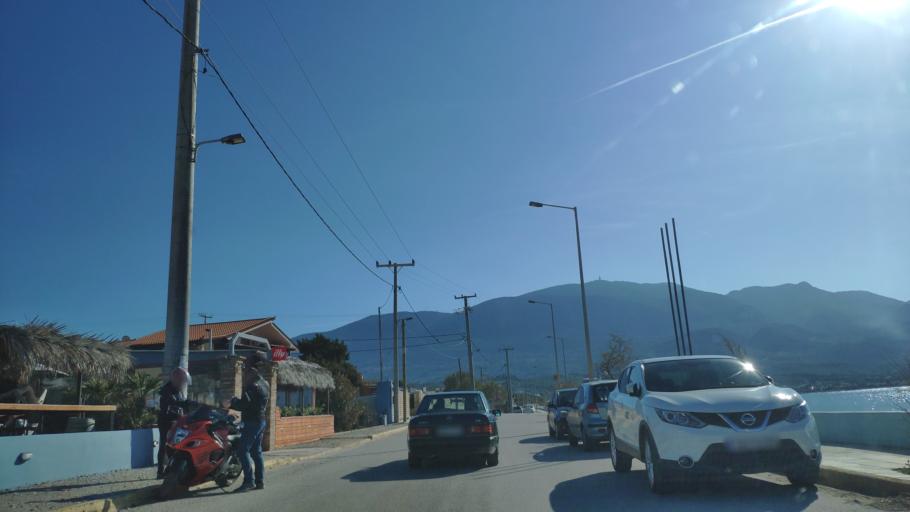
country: GR
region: Attica
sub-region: Nomarchia Dytikis Attikis
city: Kineta
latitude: 38.0838
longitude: 23.1777
